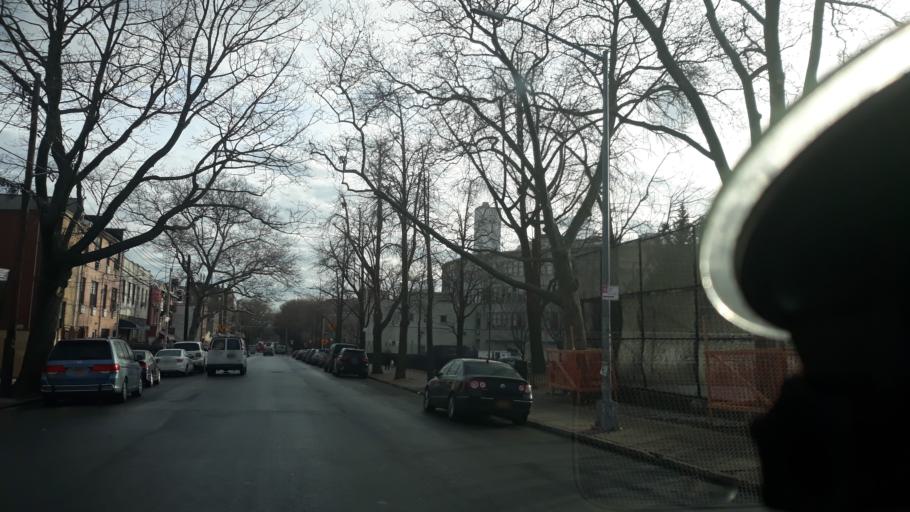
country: US
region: New York
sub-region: Kings County
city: Brooklyn
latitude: 40.6598
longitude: -73.9446
